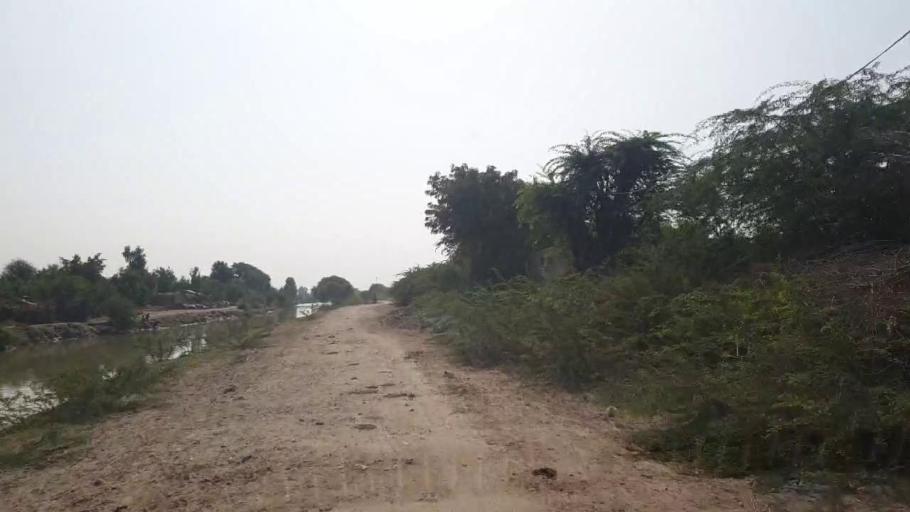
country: PK
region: Sindh
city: Badin
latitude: 24.6477
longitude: 68.8462
